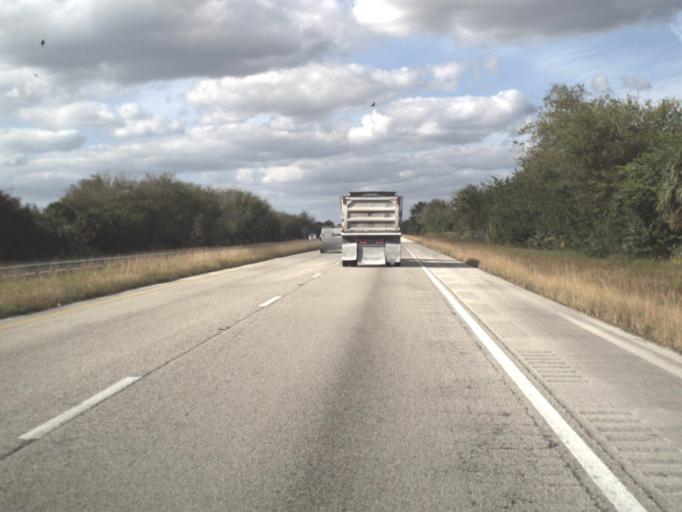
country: US
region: Florida
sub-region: Brevard County
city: Port Saint John
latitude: 28.4379
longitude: -80.8612
